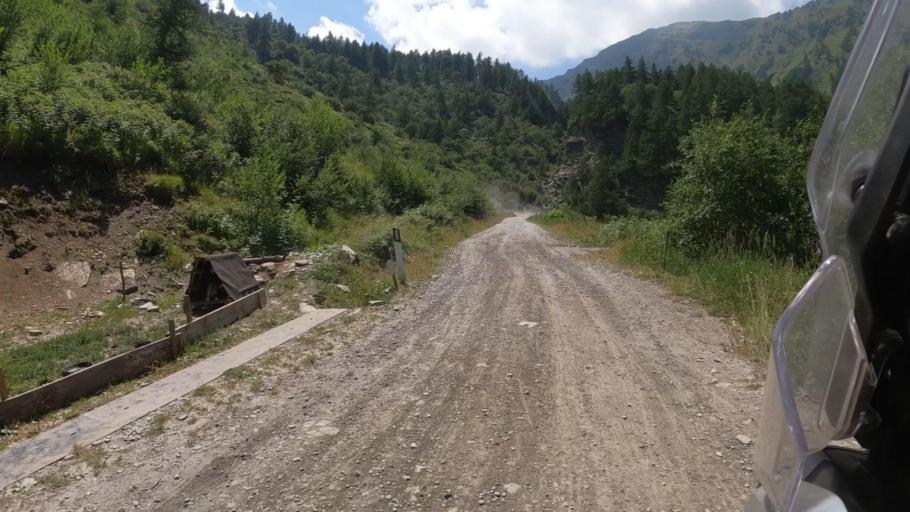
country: IT
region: Piedmont
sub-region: Provincia di Torino
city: Meana di Susa
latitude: 45.0872
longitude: 7.0621
